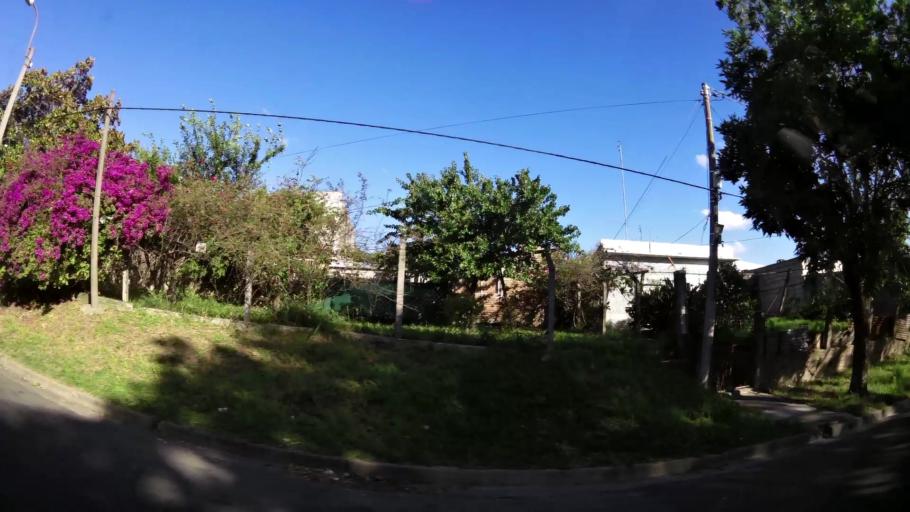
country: UY
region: Montevideo
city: Montevideo
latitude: -34.8432
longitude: -56.2437
